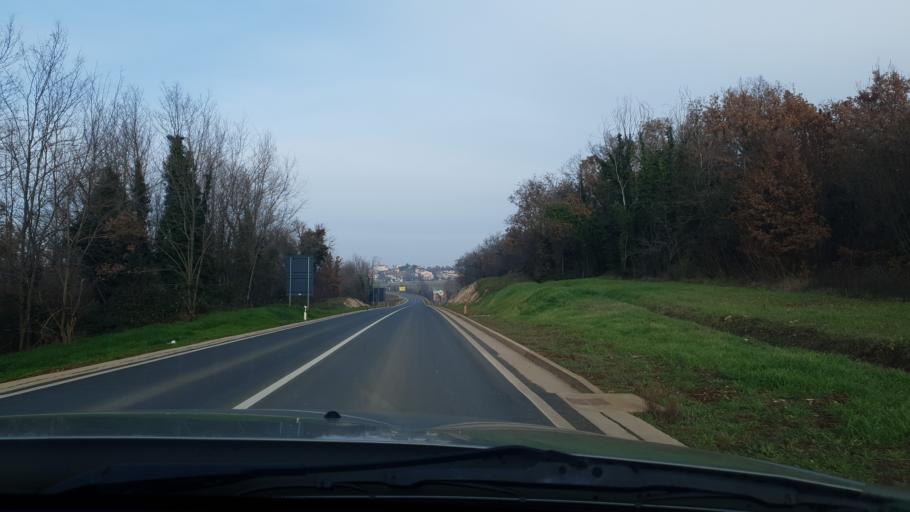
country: HR
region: Istarska
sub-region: Grad Porec
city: Porec
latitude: 45.2179
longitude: 13.6227
